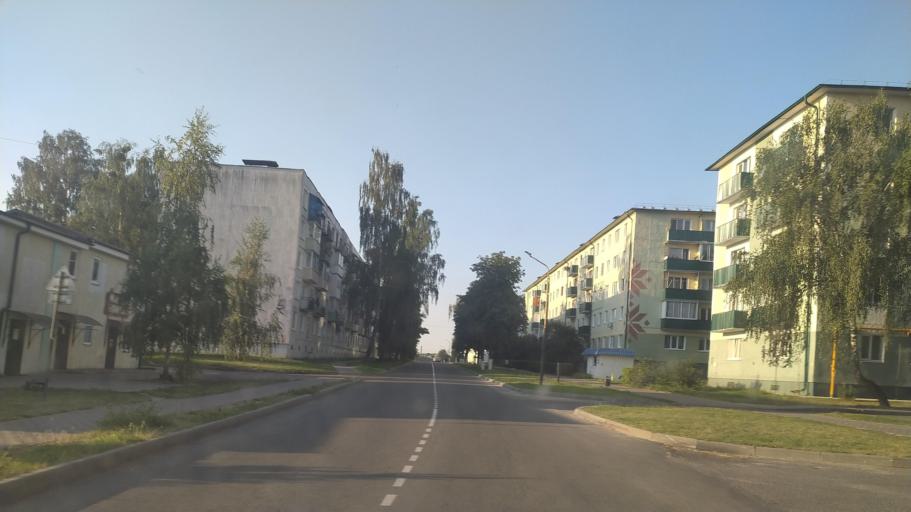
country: BY
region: Brest
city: Byaroza
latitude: 52.5428
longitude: 24.9844
